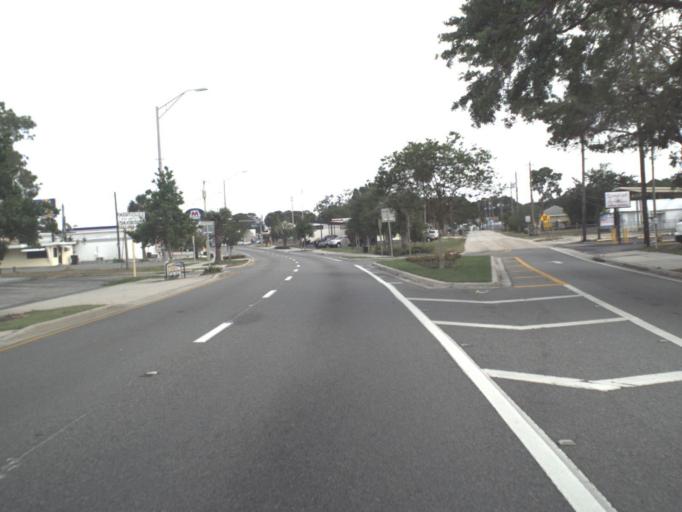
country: US
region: Florida
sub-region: Brevard County
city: Titusville
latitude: 28.6030
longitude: -80.8085
